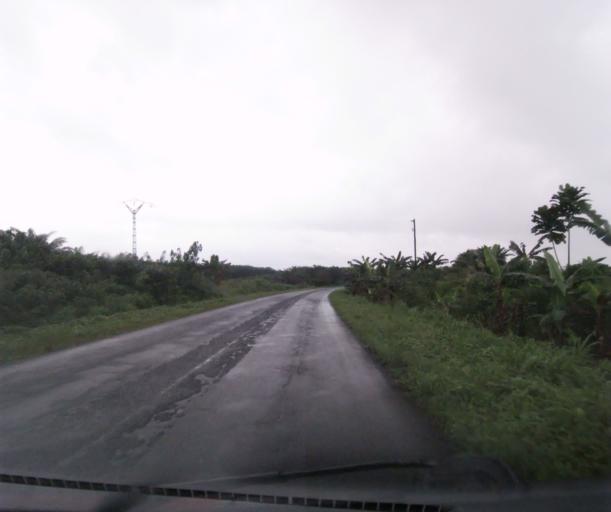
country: CM
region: South-West Province
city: Idenao
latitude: 4.1000
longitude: 8.9905
